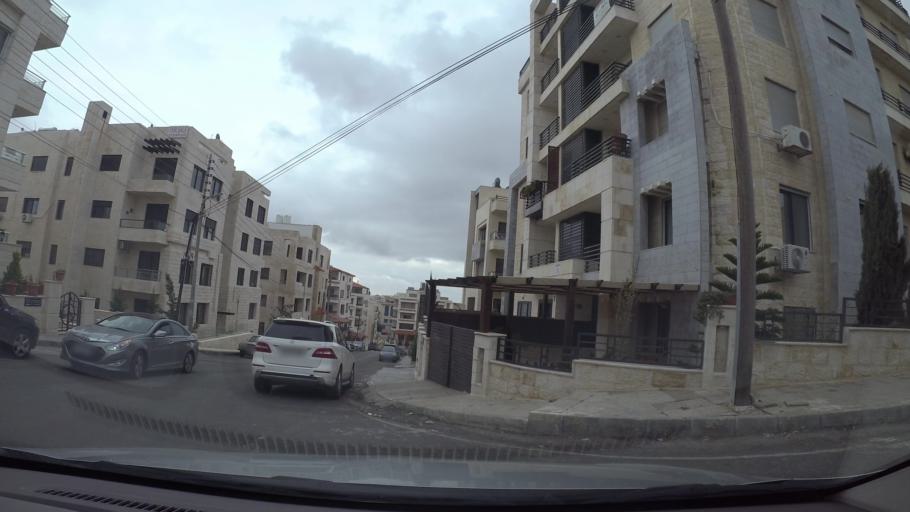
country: JO
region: Amman
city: Al Jubayhah
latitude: 31.9949
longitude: 35.8393
